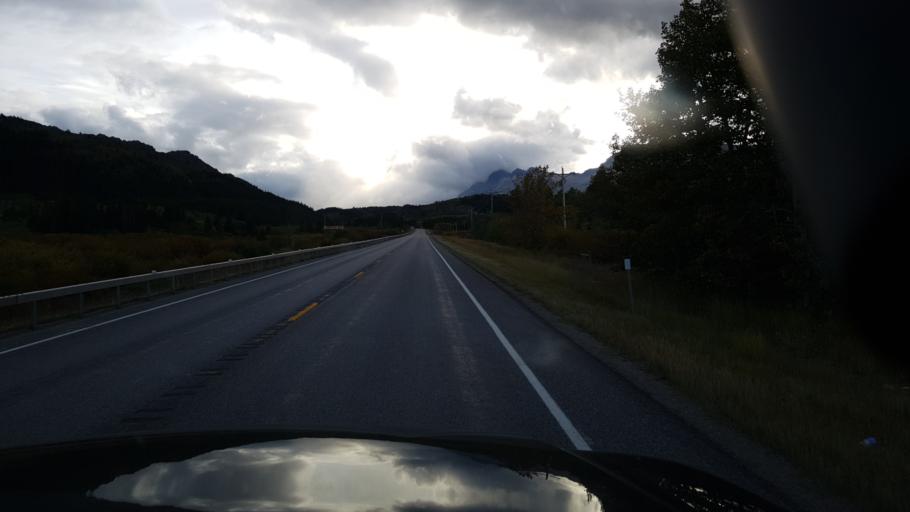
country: US
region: Montana
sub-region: Glacier County
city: South Browning
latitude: 48.4085
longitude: -113.2385
